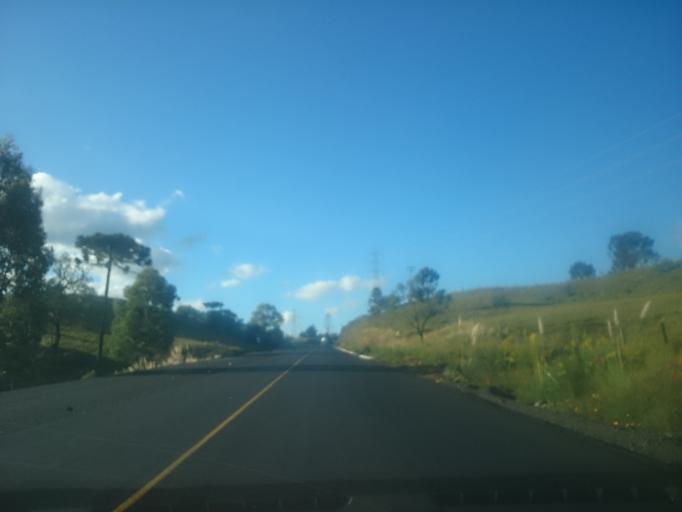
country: BR
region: Santa Catarina
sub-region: Sao Joaquim
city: Sao Joaquim
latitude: -28.0591
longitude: -50.0738
